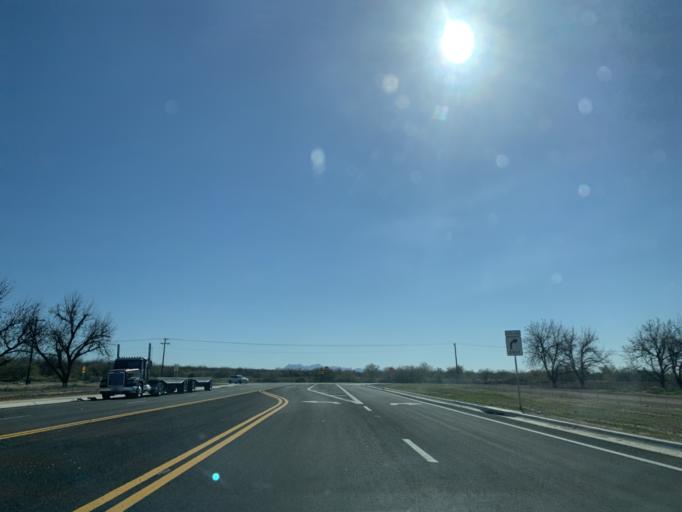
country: US
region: Arizona
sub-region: Pinal County
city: Eloy
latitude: 32.7207
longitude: -111.5176
